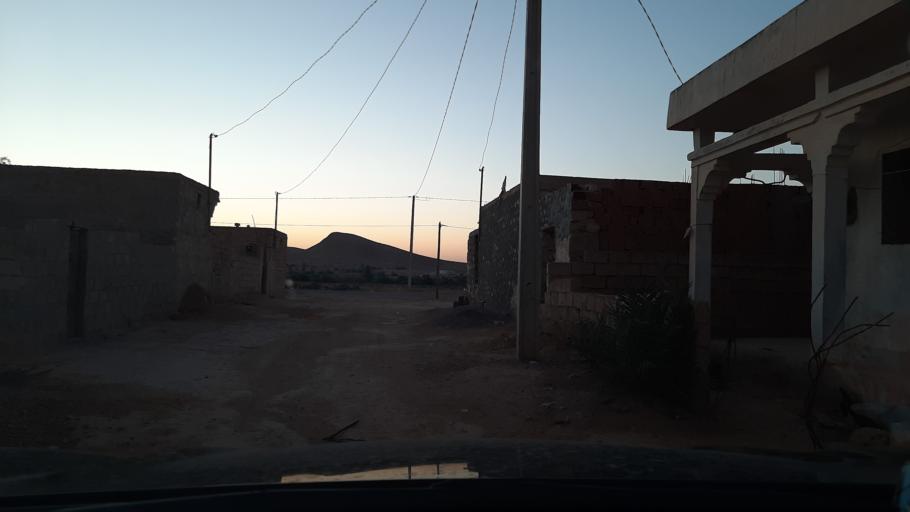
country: TN
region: Qabis
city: Matmata
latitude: 33.5701
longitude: 10.1786
